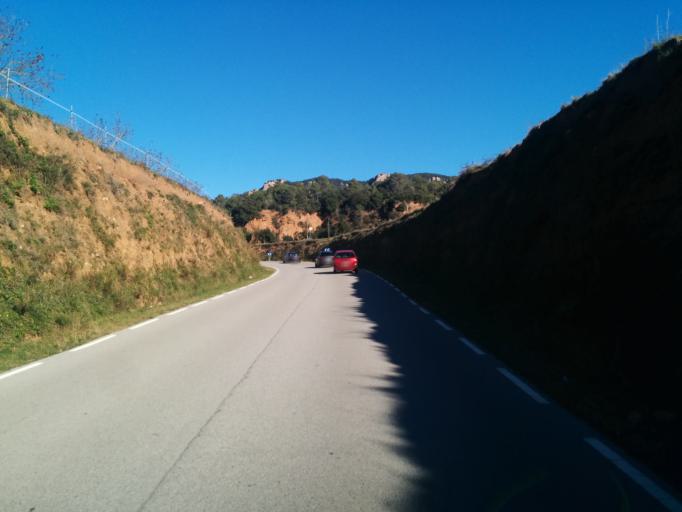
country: ES
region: Catalonia
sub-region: Provincia de Barcelona
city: Matadepera
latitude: 41.6369
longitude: 1.9939
